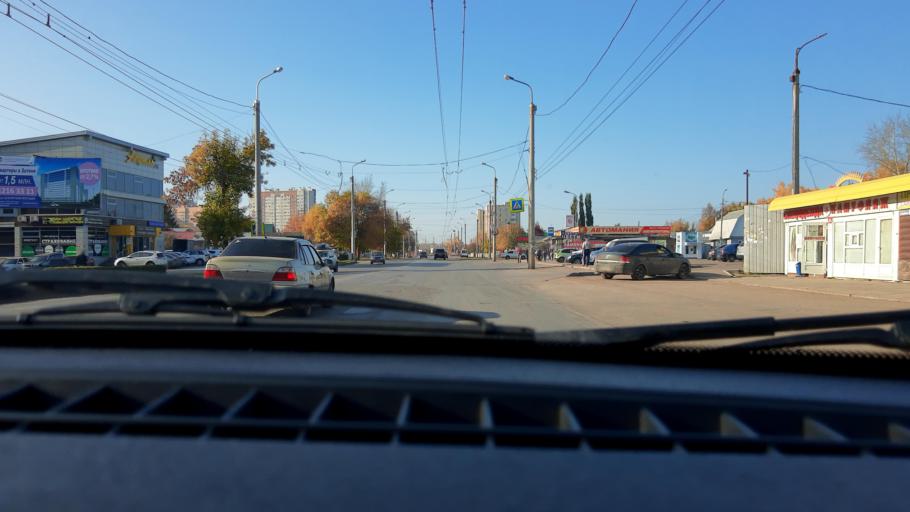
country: RU
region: Bashkortostan
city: Mikhaylovka
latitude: 54.7911
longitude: 55.8787
